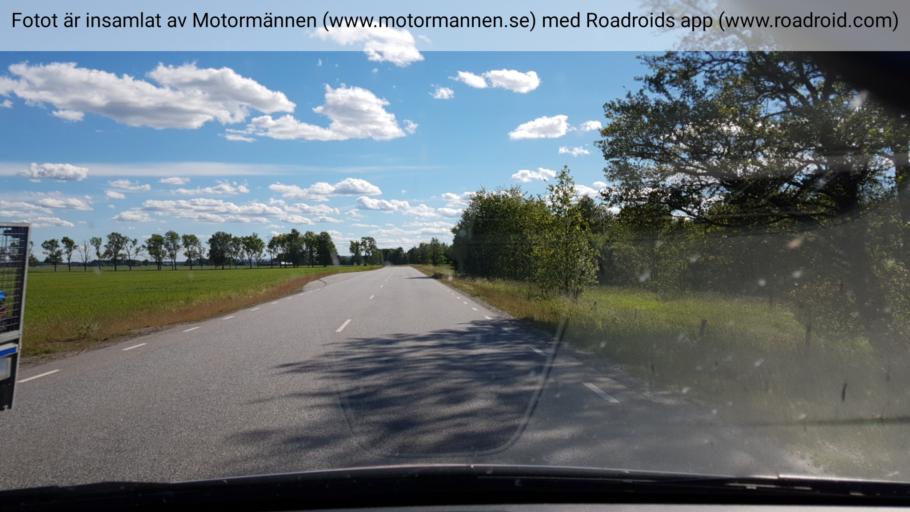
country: SE
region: Vaestra Goetaland
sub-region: Toreboda Kommun
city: Toereboda
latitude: 58.6350
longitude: 14.0242
